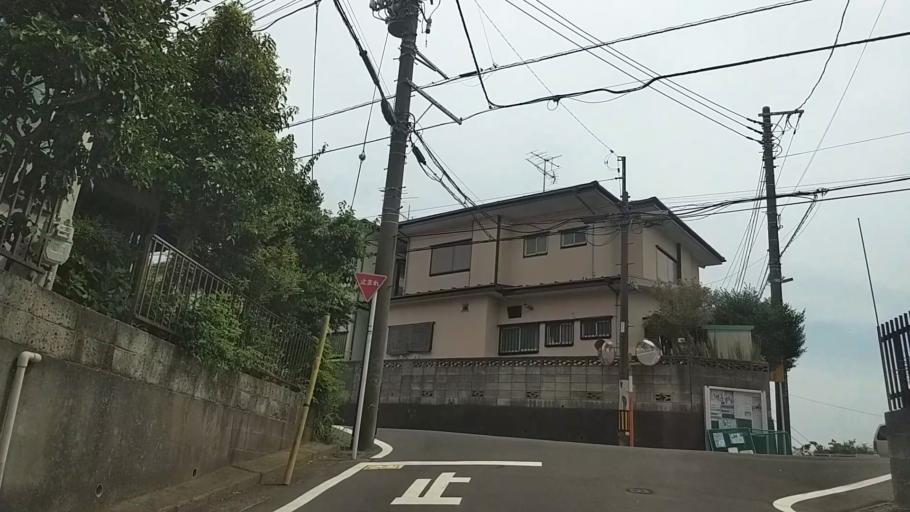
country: JP
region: Kanagawa
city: Yokohama
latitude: 35.4401
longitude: 139.6012
